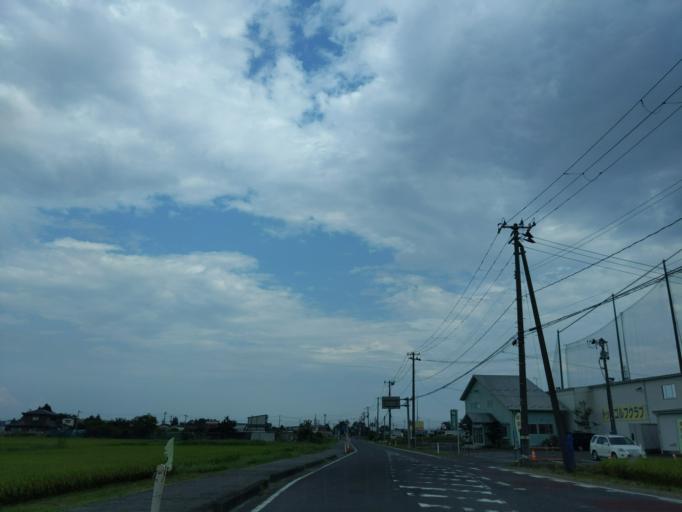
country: JP
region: Miyagi
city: Tomiya
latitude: 38.4329
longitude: 140.8854
